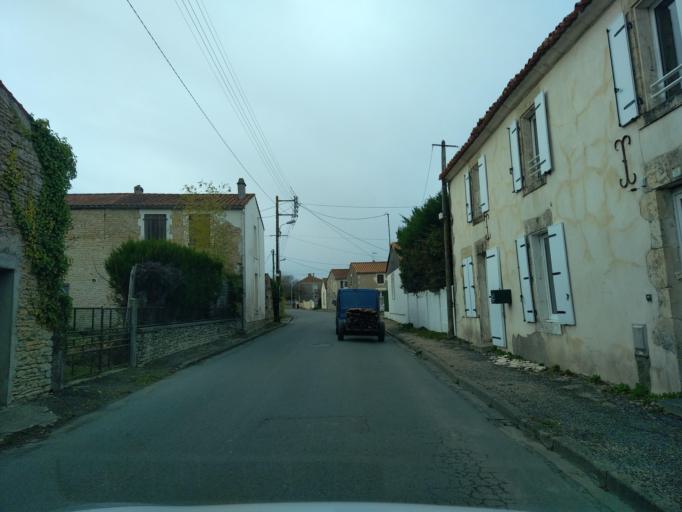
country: FR
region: Pays de la Loire
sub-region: Departement de la Vendee
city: Vix
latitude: 46.3664
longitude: -0.8633
